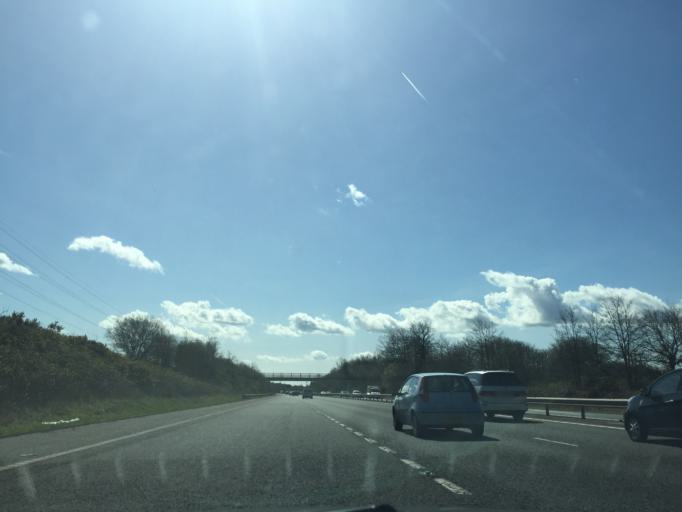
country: GB
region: England
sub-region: Hampshire
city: Cowplain
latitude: 50.9029
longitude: -0.9988
